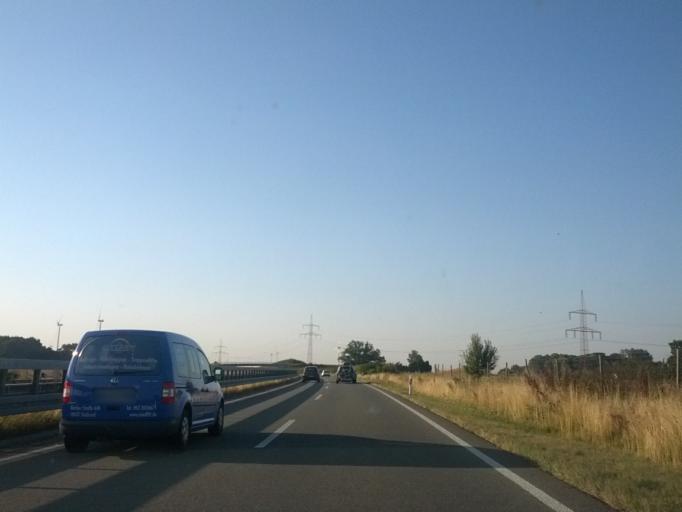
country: DE
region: Mecklenburg-Vorpommern
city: Brandshagen
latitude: 54.2096
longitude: 13.1507
